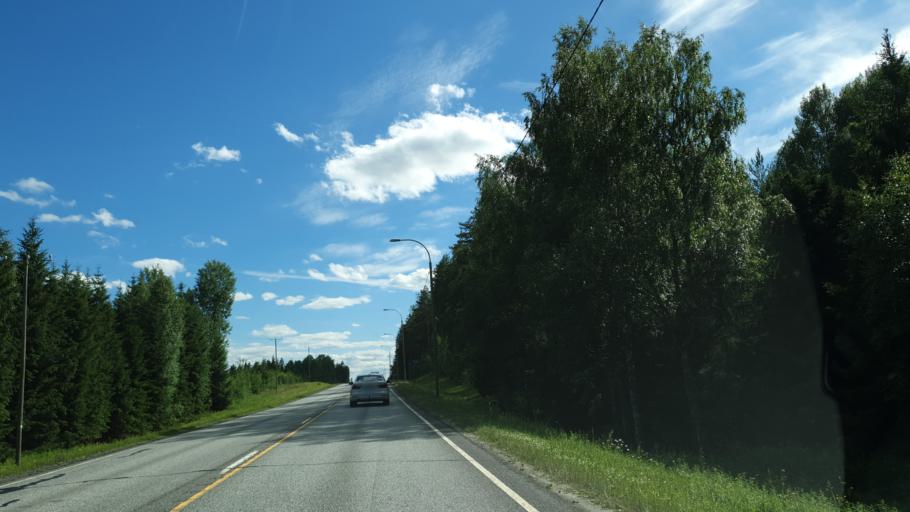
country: FI
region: Southern Savonia
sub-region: Pieksaemaeki
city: Juva
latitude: 61.9110
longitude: 27.8055
